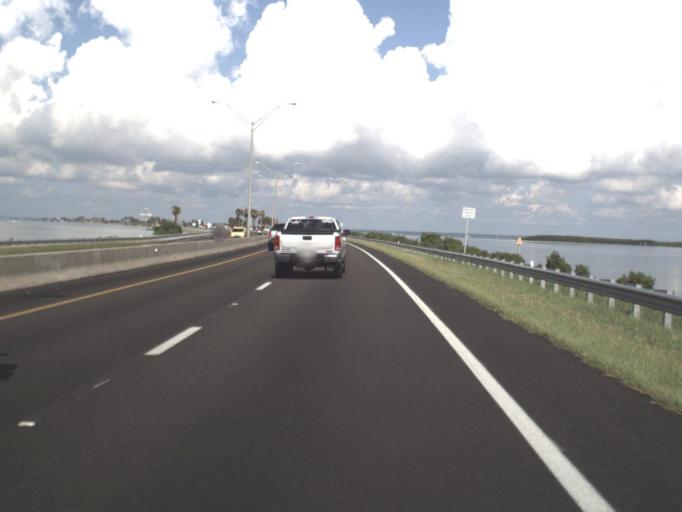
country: US
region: Florida
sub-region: Hillsborough County
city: Town 'n' Country
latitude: 27.9729
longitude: -82.5848
